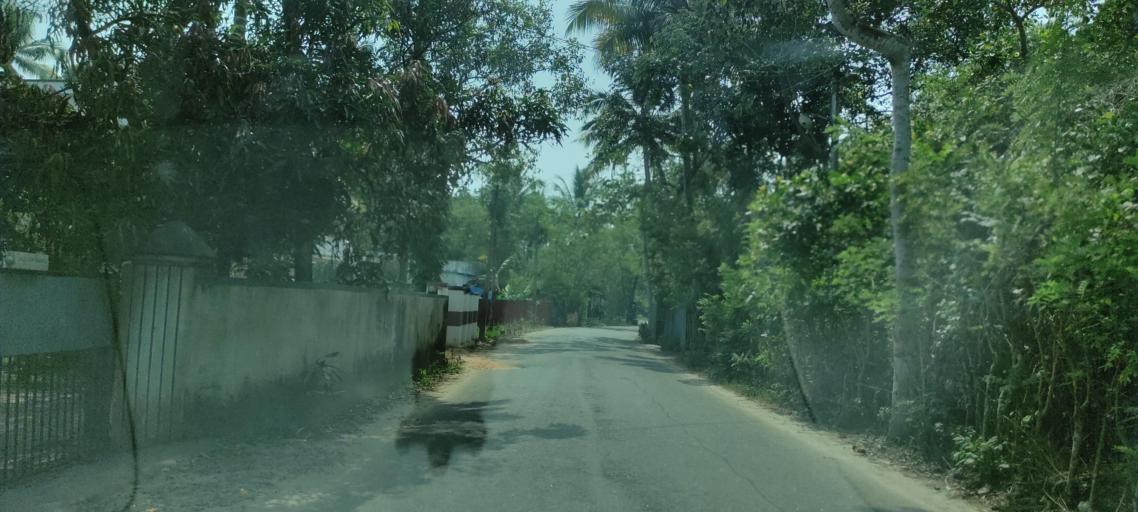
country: IN
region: Kerala
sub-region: Alappuzha
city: Shertallai
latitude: 9.6470
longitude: 76.3556
